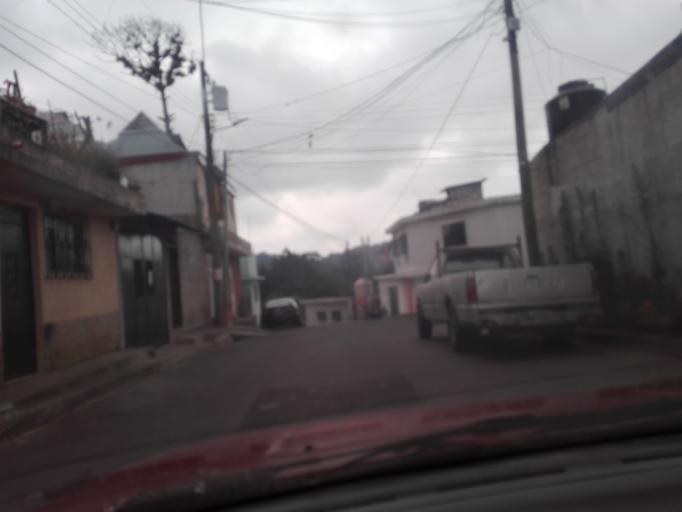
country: GT
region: Guatemala
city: San Jose Pinula
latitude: 14.5736
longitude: -90.4482
